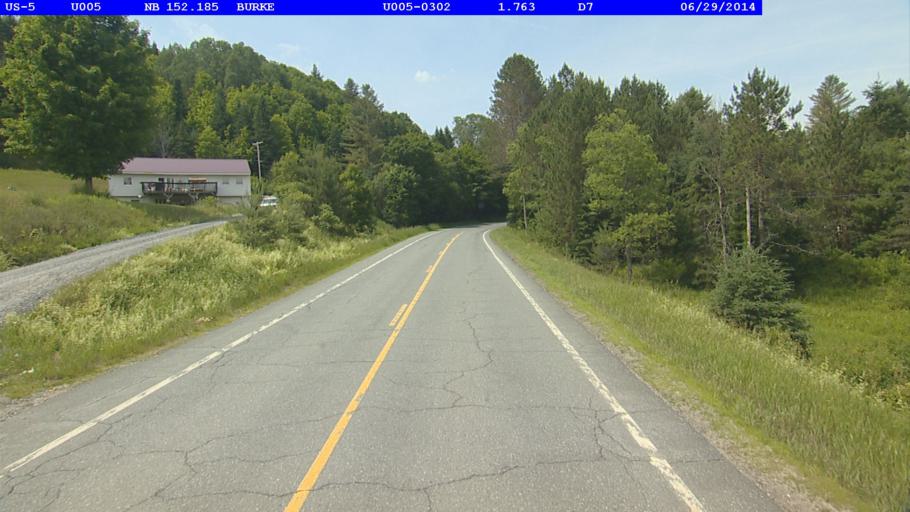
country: US
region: Vermont
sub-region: Caledonia County
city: Lyndonville
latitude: 44.6102
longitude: -71.9725
